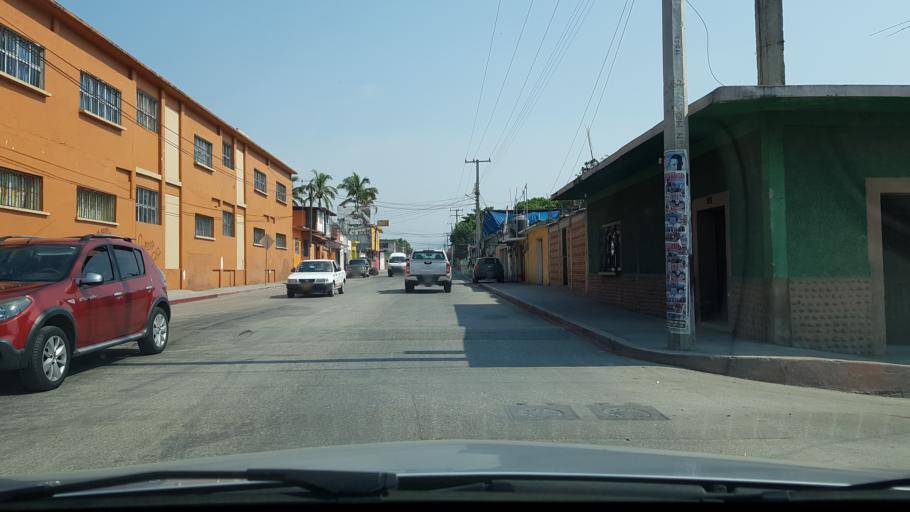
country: MX
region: Morelos
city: Zacatepec
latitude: 18.6595
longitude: -99.1864
